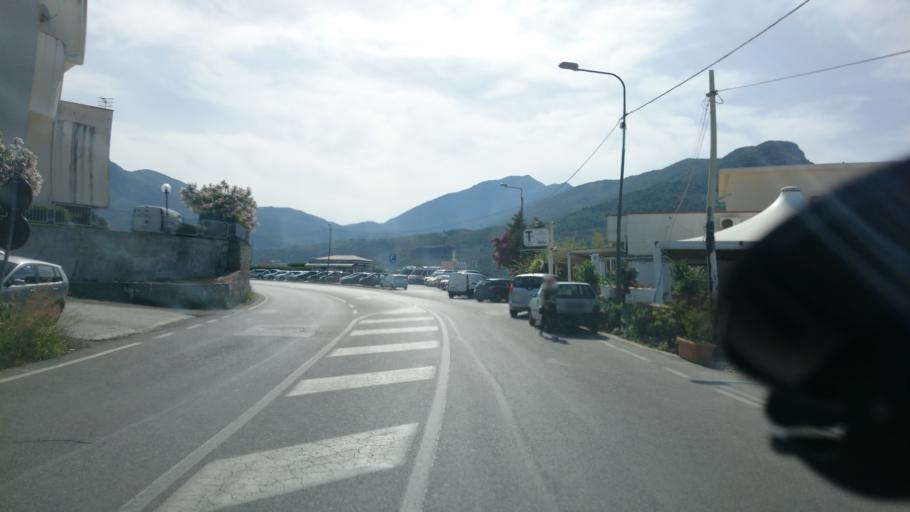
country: IT
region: Campania
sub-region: Provincia di Salerno
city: Sapri
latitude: 40.0692
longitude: 15.6170
